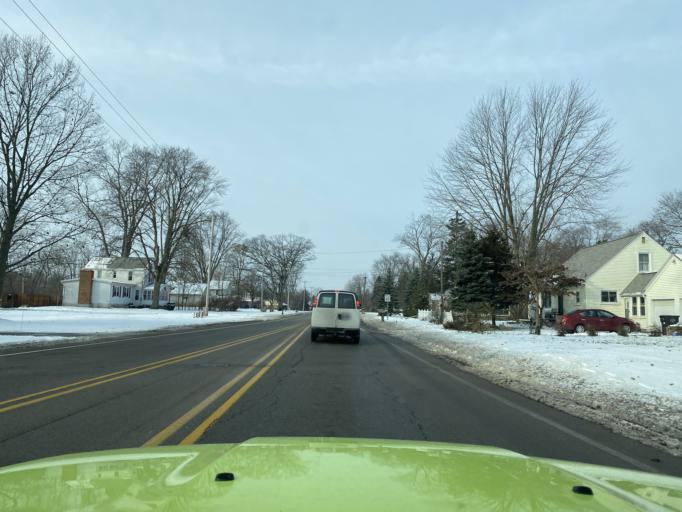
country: US
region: Michigan
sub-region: Ottawa County
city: Hudsonville
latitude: 42.8854
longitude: -85.8823
